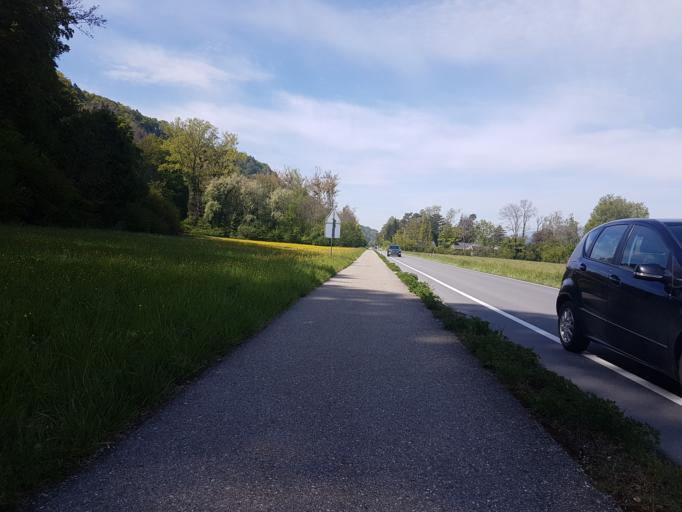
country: CH
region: Bern
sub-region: Seeland District
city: Erlach
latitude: 47.0442
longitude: 7.1439
